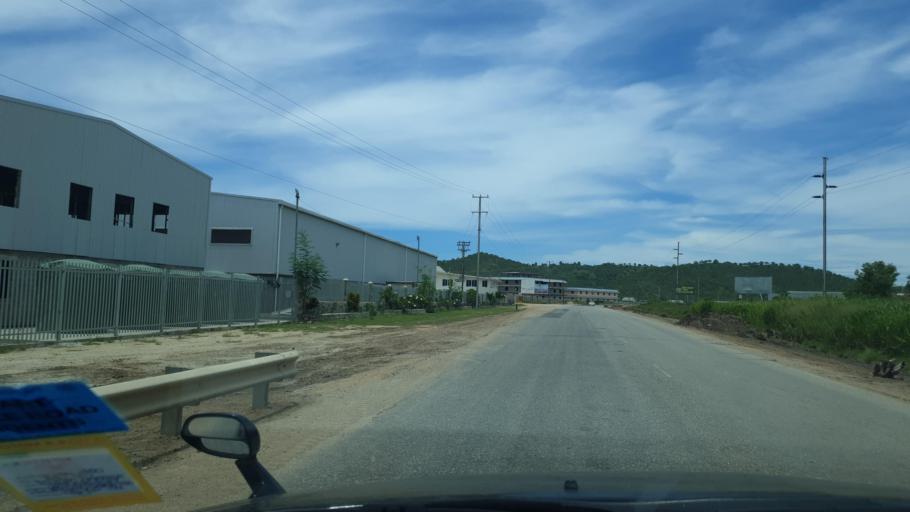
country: PG
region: National Capital
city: Port Moresby
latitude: -9.4196
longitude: 147.0831
